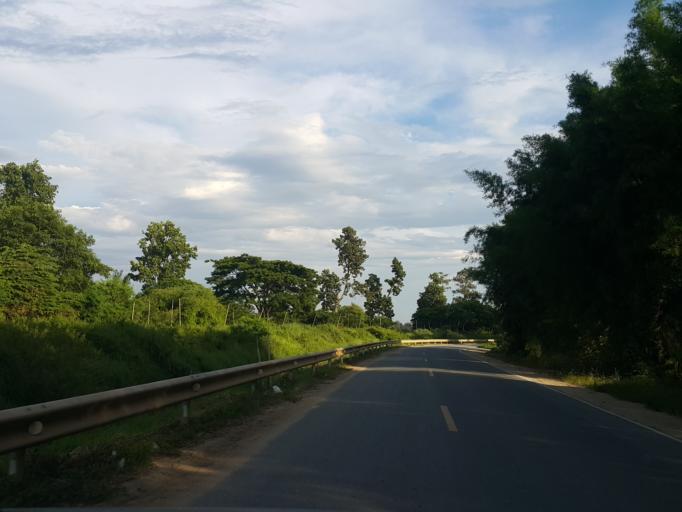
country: TH
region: Chiang Mai
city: San Sai
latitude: 18.9262
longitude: 98.9998
